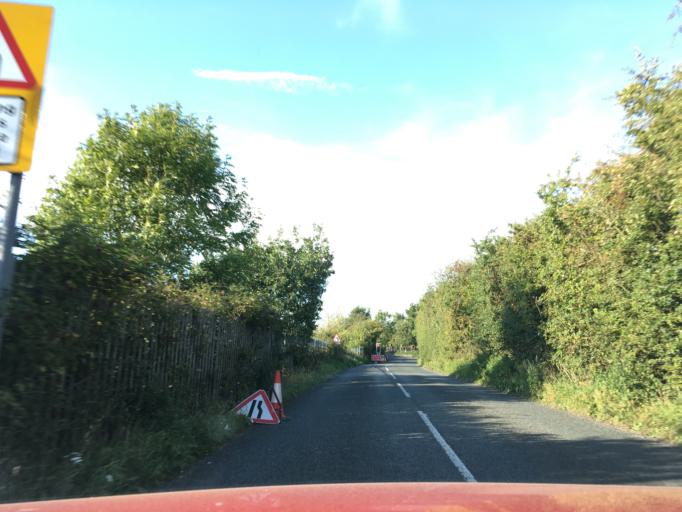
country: GB
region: England
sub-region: South Gloucestershire
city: Yate
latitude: 51.5296
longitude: -2.4376
